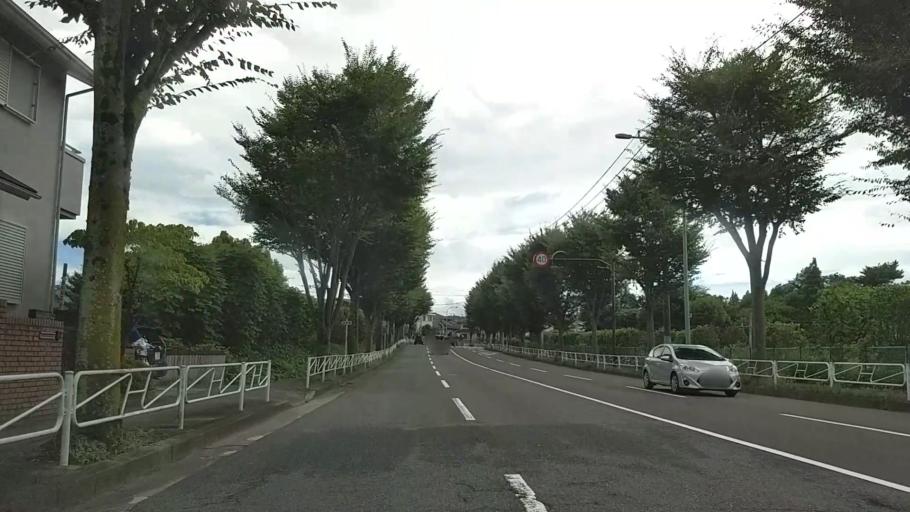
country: JP
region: Tokyo
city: Hachioji
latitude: 35.6364
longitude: 139.3569
